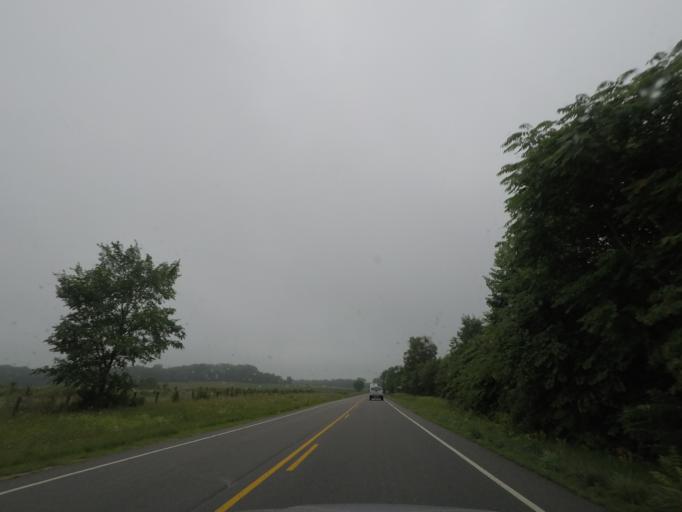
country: US
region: Virginia
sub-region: Buckingham County
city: Buckingham
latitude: 37.4397
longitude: -78.4533
